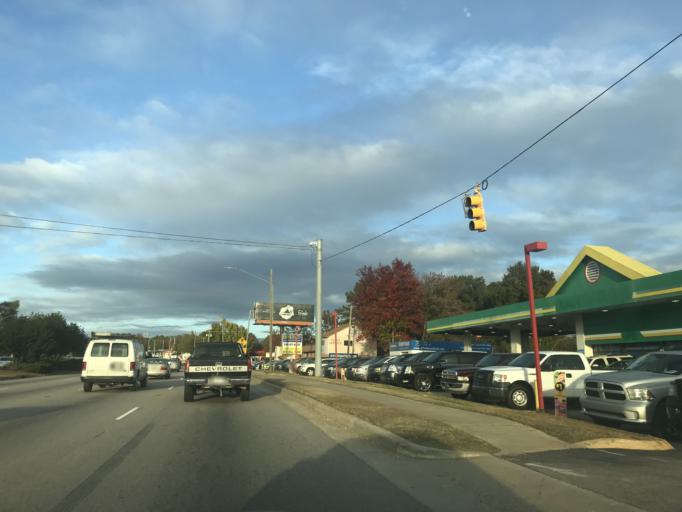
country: US
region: North Carolina
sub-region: Wake County
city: Raleigh
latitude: 35.8223
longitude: -78.5890
